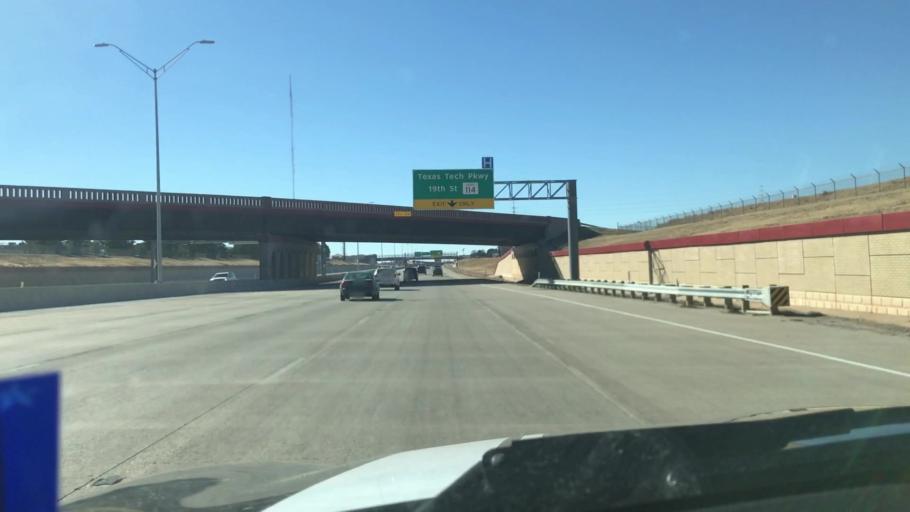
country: US
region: Texas
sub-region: Lubbock County
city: Lubbock
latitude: 33.5882
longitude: -101.8835
